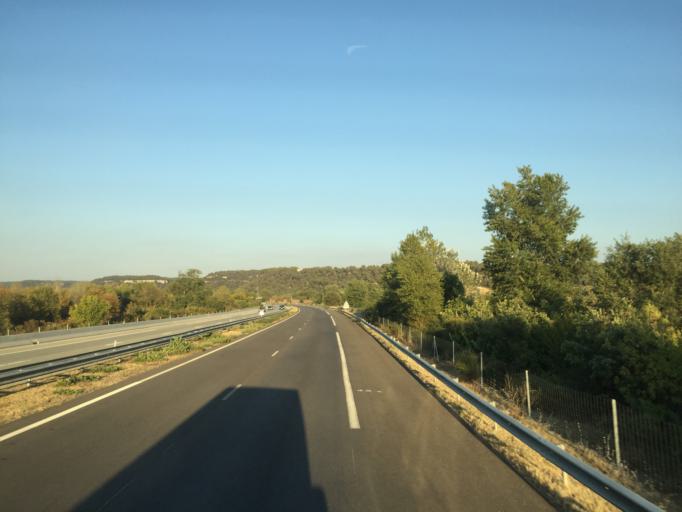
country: FR
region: Provence-Alpes-Cote d'Azur
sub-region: Departement des Bouches-du-Rhone
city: Peyrolles-en-Provence
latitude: 43.6561
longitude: 5.6009
